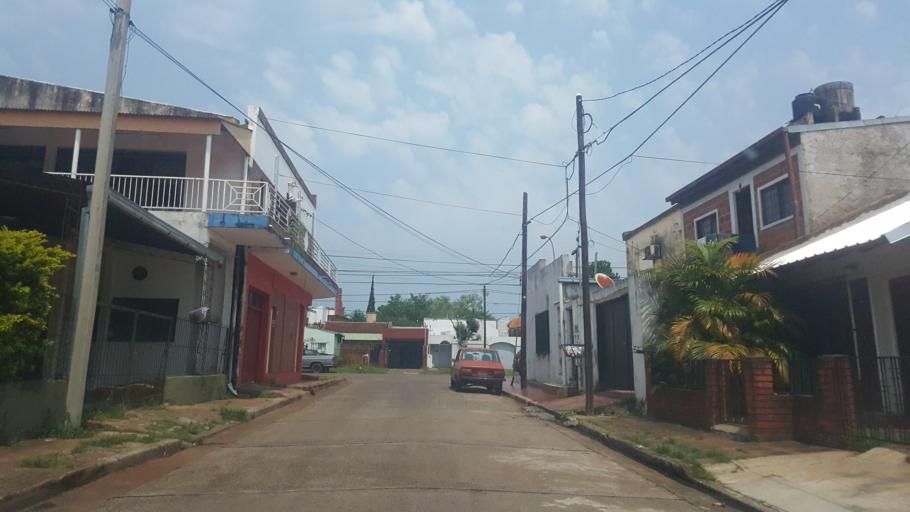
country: AR
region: Misiones
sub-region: Departamento de Capital
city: Posadas
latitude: -27.3686
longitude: -55.9158
